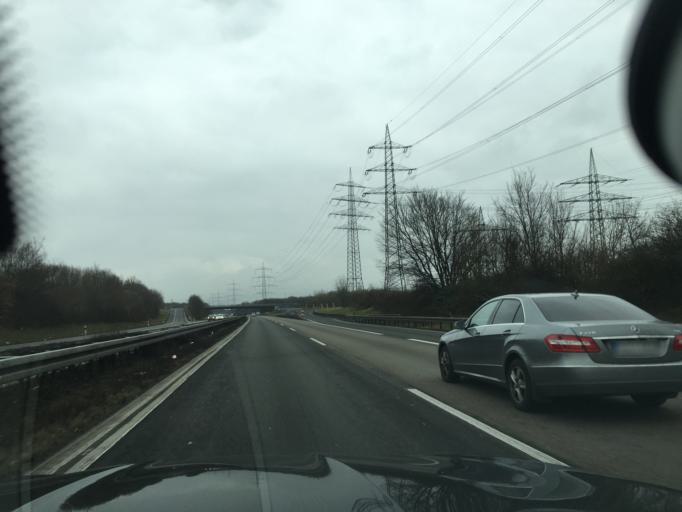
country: DE
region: North Rhine-Westphalia
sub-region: Regierungsbezirk Koln
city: Wahn-Heide
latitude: 50.8206
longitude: 7.1064
